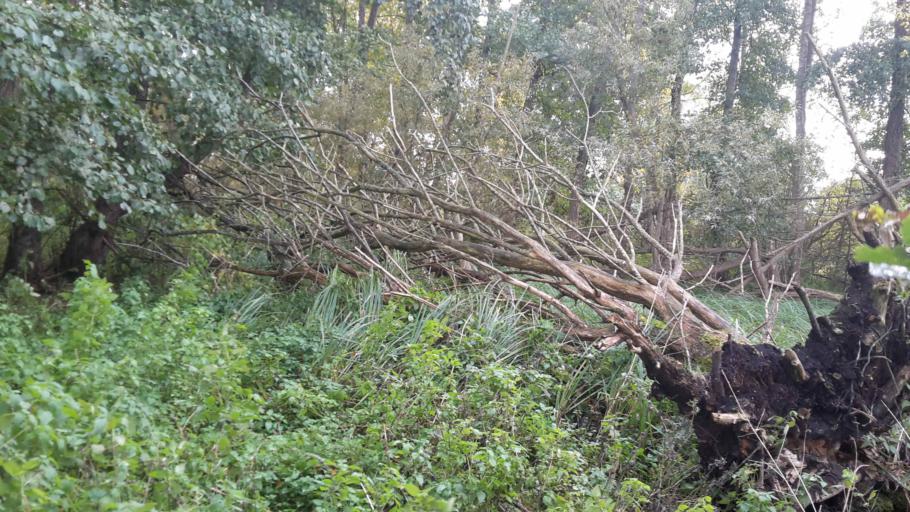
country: DK
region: Capital Region
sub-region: Egedal Kommune
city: Smorumnedre
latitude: 55.7627
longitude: 12.2998
